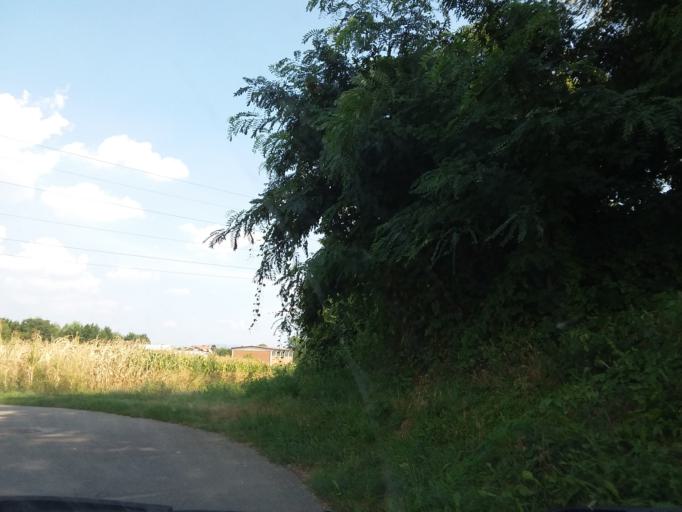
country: IT
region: Piedmont
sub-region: Provincia di Torino
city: Pianezza
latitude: 45.0866
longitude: 7.5442
